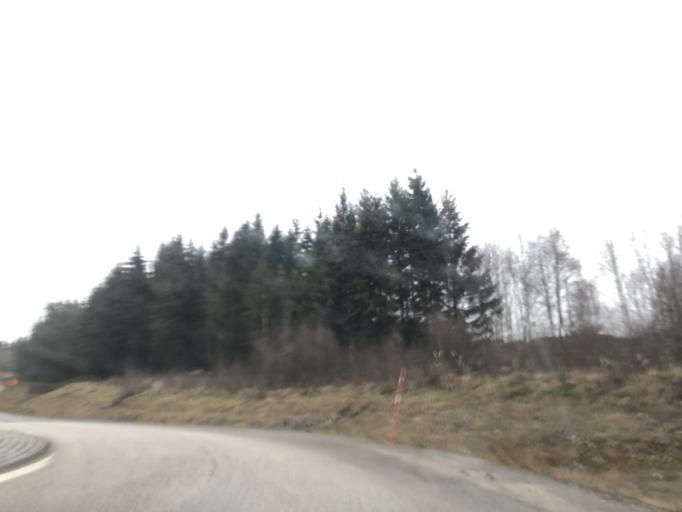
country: SE
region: Vaestra Goetaland
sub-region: Ulricehamns Kommun
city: Ulricehamn
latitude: 57.8177
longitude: 13.2863
